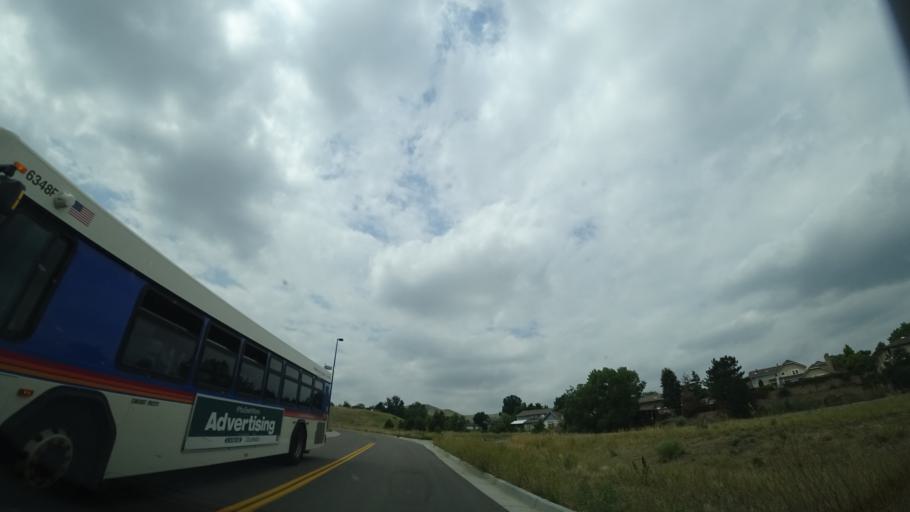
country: US
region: Colorado
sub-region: Jefferson County
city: West Pleasant View
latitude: 39.7154
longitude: -105.1531
